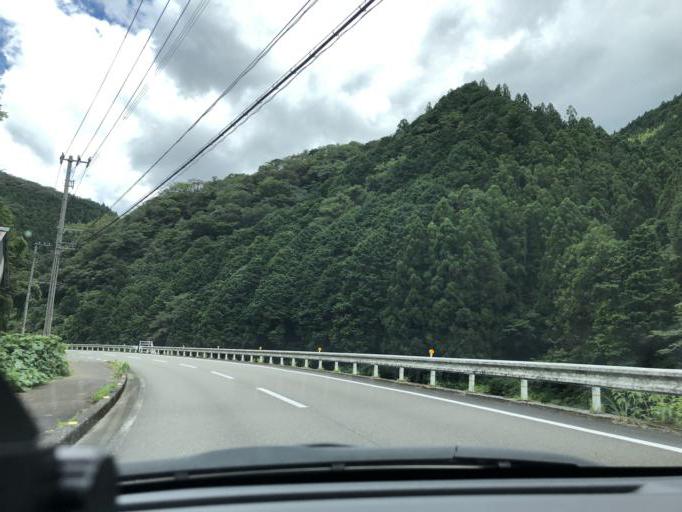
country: JP
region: Kochi
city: Kochi-shi
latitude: 33.6328
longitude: 133.5229
